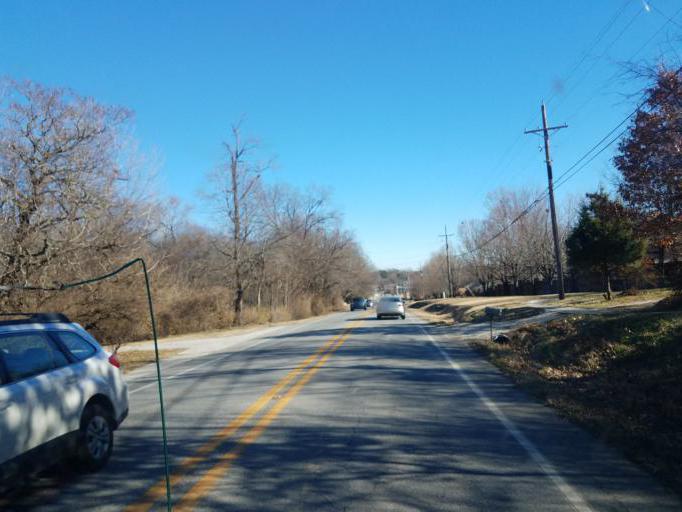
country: US
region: Arkansas
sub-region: Washington County
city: Fayetteville
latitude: 36.0876
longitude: -94.1287
